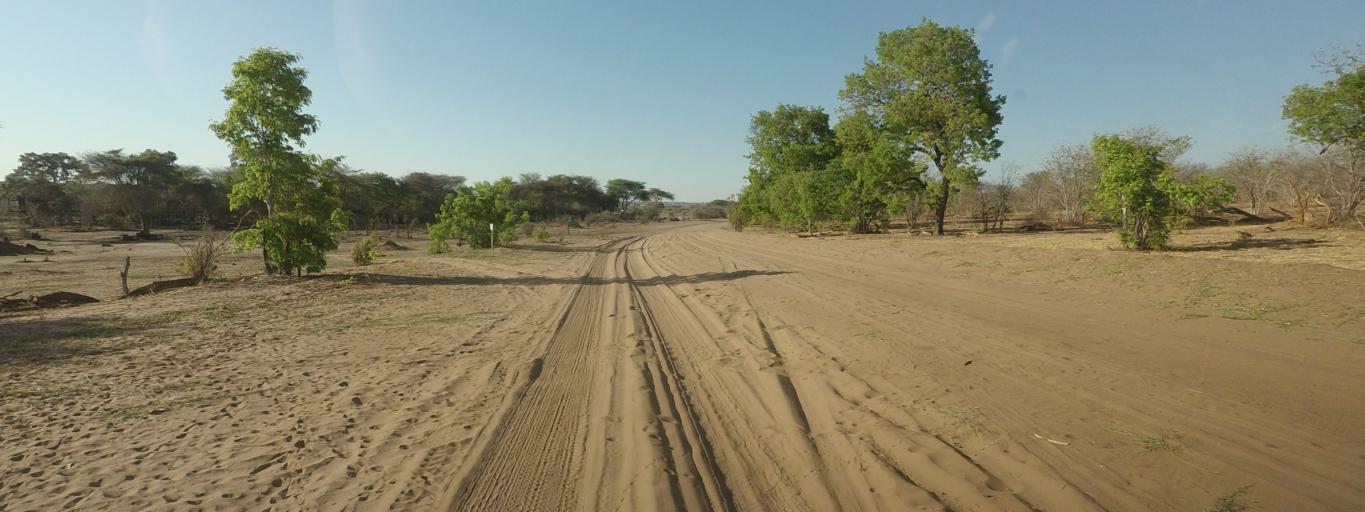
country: BW
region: North West
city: Kasane
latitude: -17.8785
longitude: 25.2344
